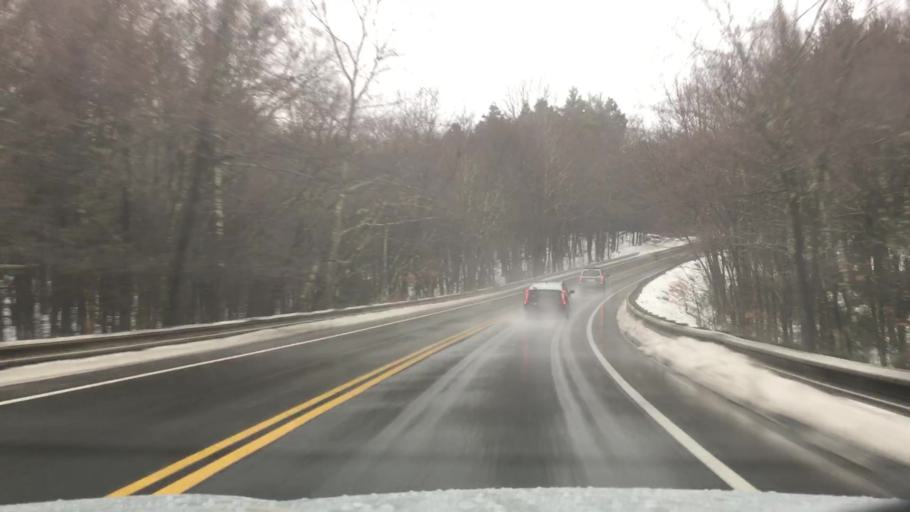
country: US
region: Massachusetts
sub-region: Franklin County
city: Shutesbury
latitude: 42.4384
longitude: -72.3897
